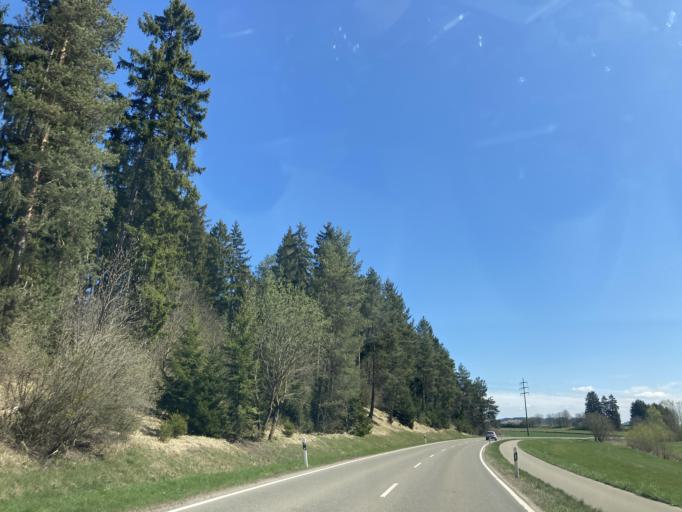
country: DE
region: Baden-Wuerttemberg
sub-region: Freiburg Region
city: Villingen-Schwenningen
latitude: 48.0314
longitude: 8.4972
